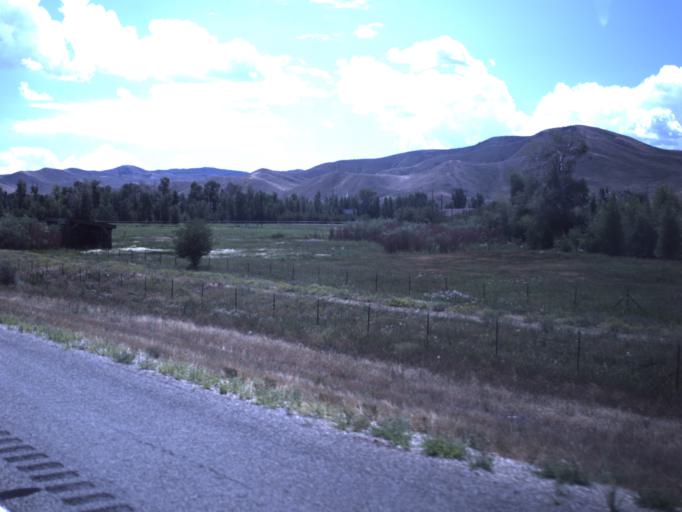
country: US
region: Utah
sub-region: Summit County
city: Coalville
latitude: 41.0321
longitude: -111.5049
